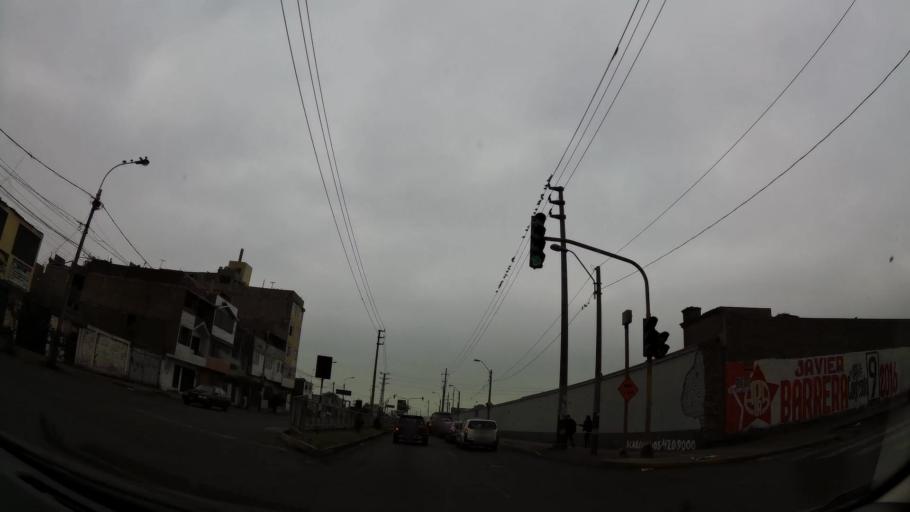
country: PE
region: Lima
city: Lima
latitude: -12.0415
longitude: -77.0038
